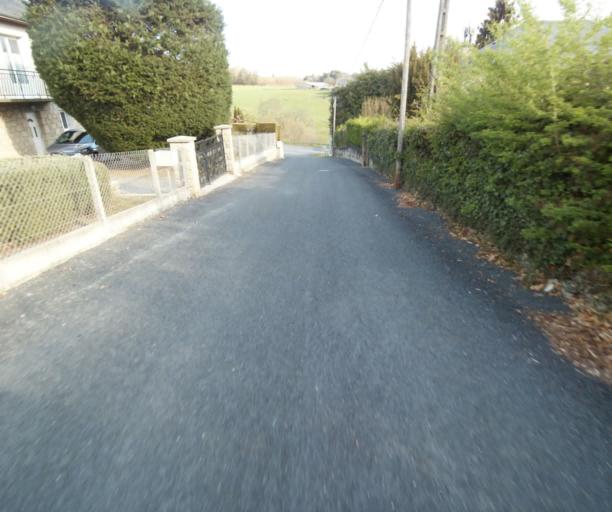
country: FR
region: Limousin
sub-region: Departement de la Correze
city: Correze
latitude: 45.3755
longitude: 1.8706
